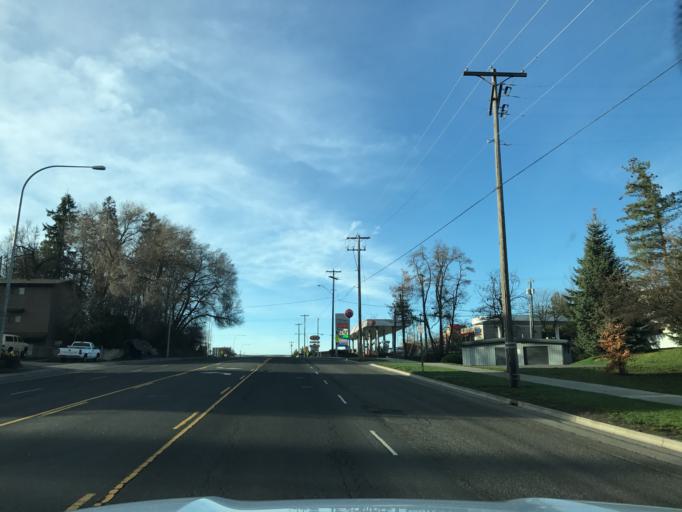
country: US
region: Idaho
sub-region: Latah County
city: Moscow
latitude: 46.7237
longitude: -117.0015
